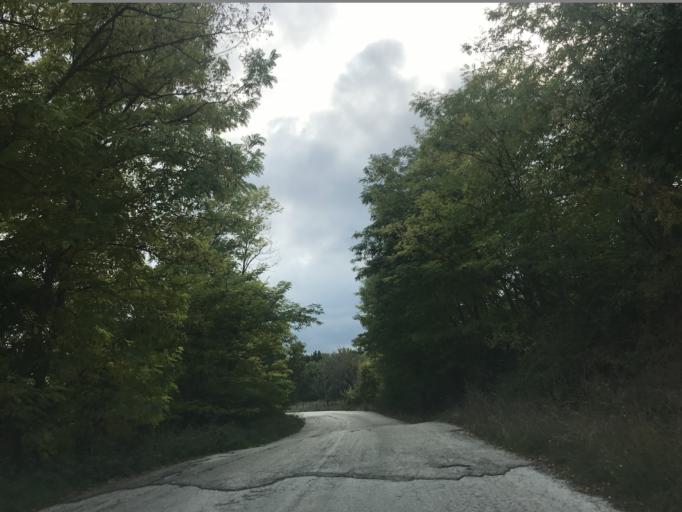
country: IT
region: Molise
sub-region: Provincia di Isernia
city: Bagnoli del Trigno
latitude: 41.6842
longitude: 14.4568
